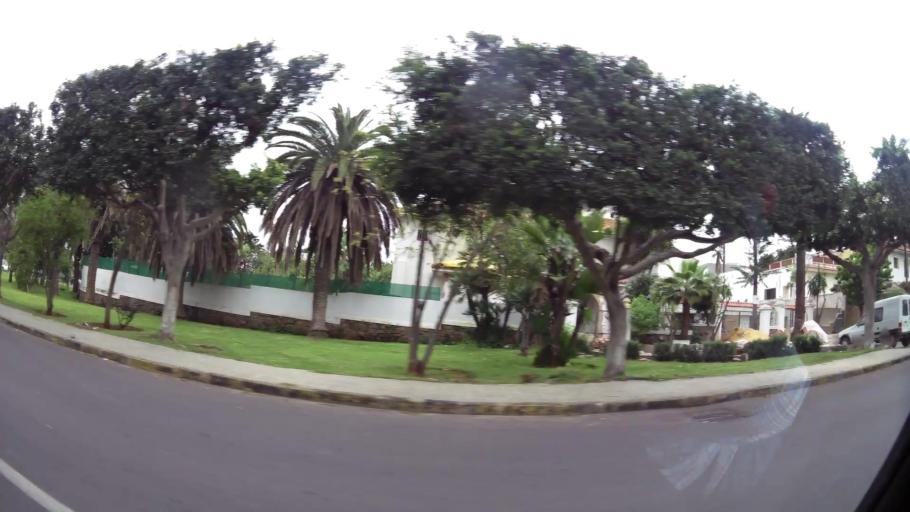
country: MA
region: Grand Casablanca
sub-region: Casablanca
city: Casablanca
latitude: 33.5831
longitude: -7.6625
